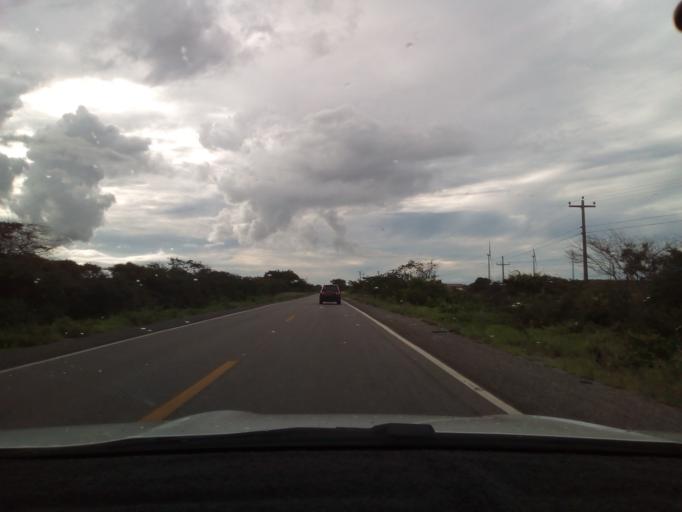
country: BR
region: Ceara
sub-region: Aracati
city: Aracati
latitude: -4.6328
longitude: -37.6388
